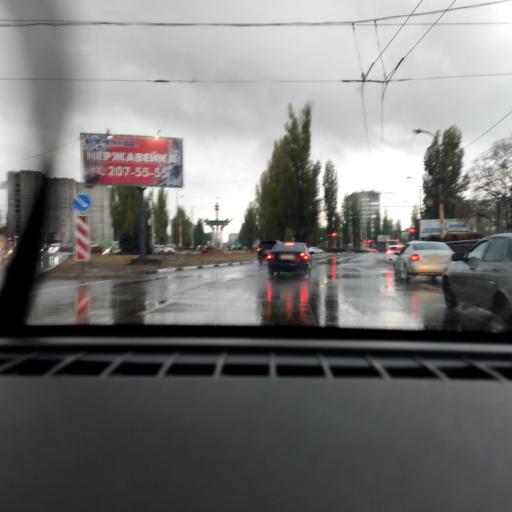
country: RU
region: Voronezj
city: Voronezh
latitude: 51.6876
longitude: 39.2653
